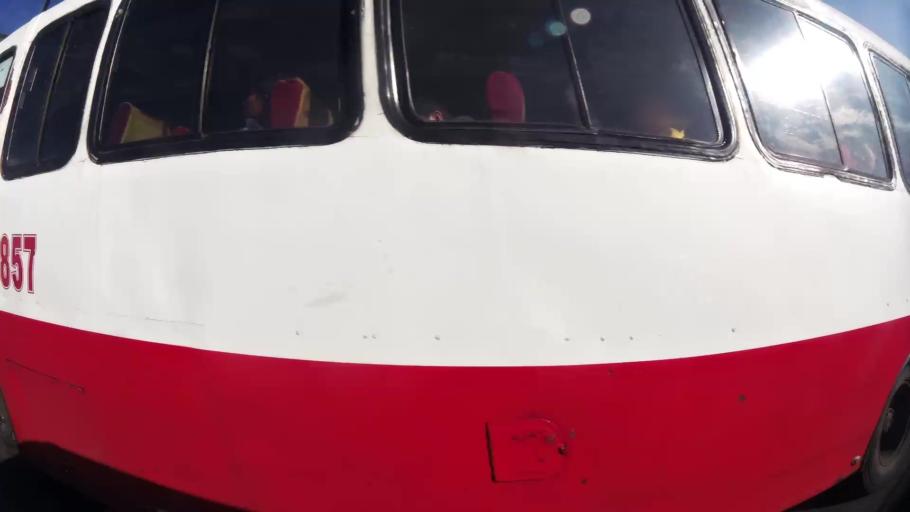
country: EC
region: Pichincha
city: Quito
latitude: -0.2421
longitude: -78.5127
